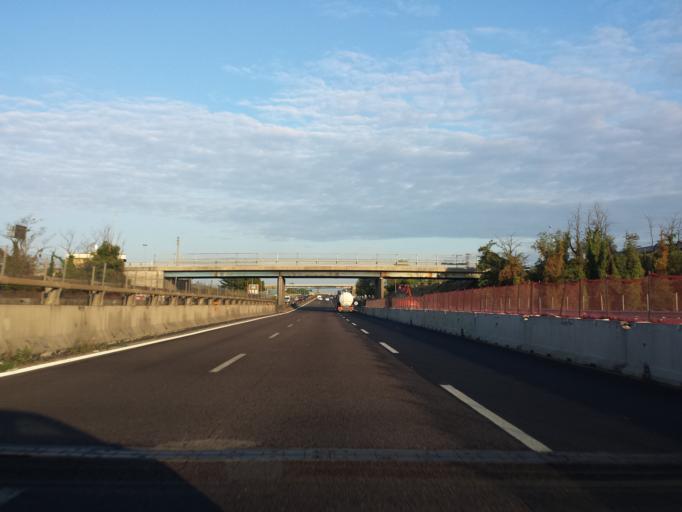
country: IT
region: Lombardy
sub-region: Provincia di Bergamo
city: Castelli Calepio
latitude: 45.6229
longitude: 9.9013
